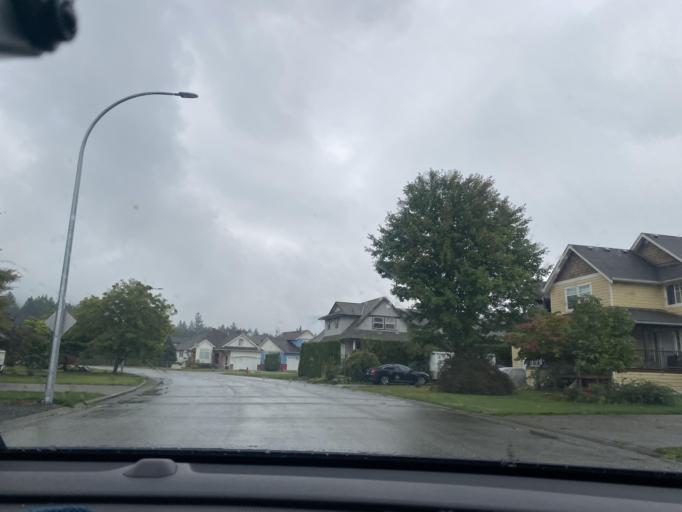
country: CA
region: British Columbia
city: Agassiz
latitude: 49.2976
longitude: -121.7807
